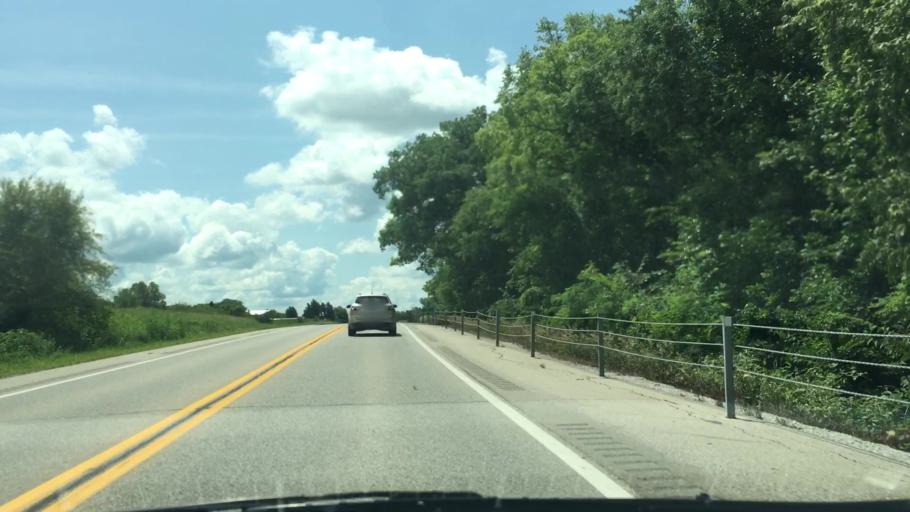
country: US
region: Iowa
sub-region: Johnson County
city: Solon
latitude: 41.7447
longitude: -91.4739
